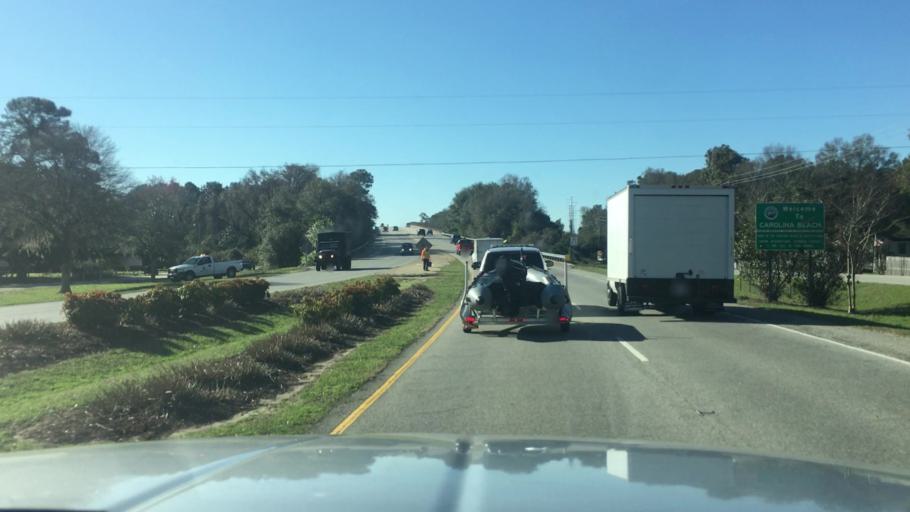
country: US
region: North Carolina
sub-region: New Hanover County
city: Sea Breeze
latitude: 34.0613
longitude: -77.8994
